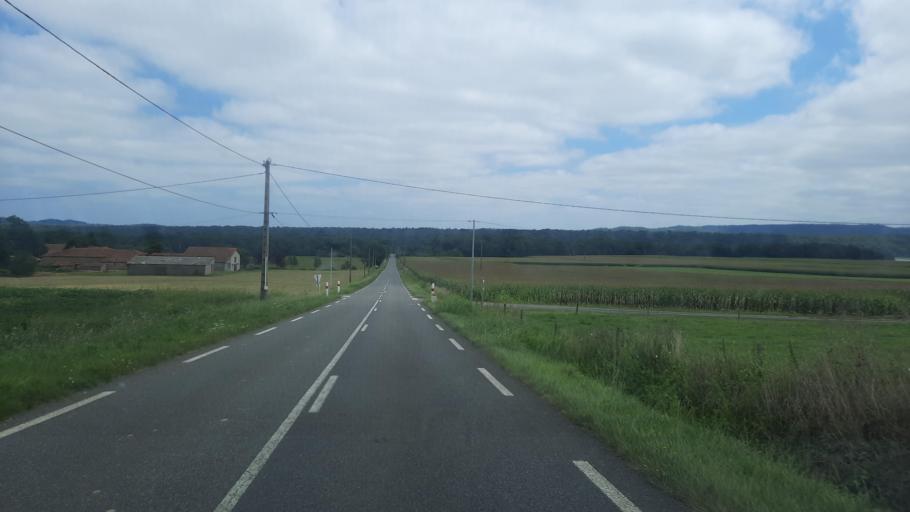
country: FR
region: Midi-Pyrenees
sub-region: Departement des Hautes-Pyrenees
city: Trie-sur-Baise
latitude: 43.3005
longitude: 0.4094
